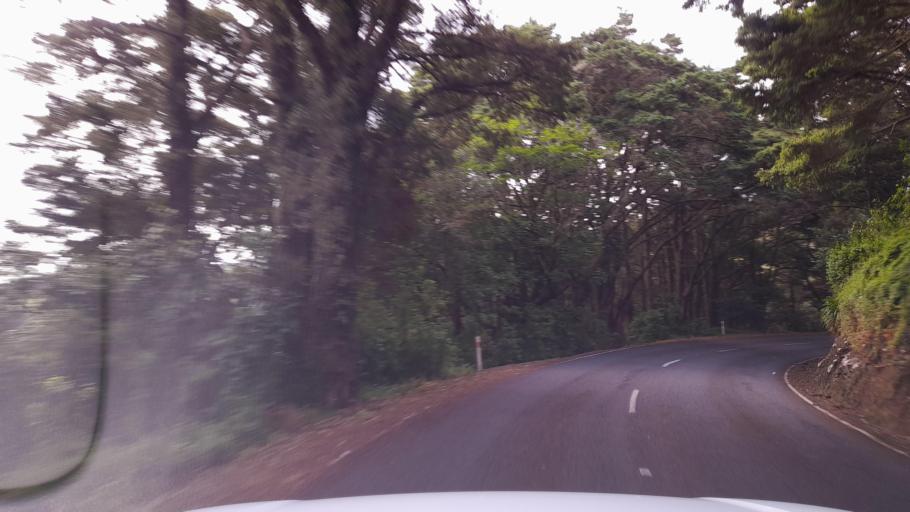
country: NZ
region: Northland
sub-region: Whangarei
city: Maungatapere
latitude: -35.7529
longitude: 174.2497
